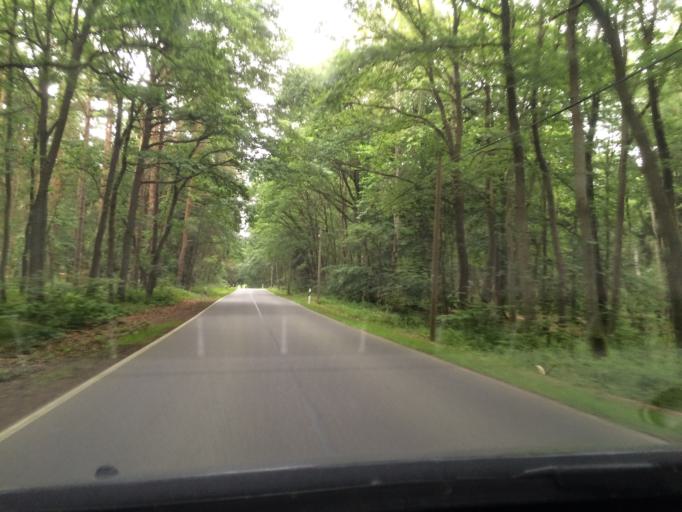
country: DE
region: Mecklenburg-Vorpommern
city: Prohn
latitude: 54.4274
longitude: 13.0252
